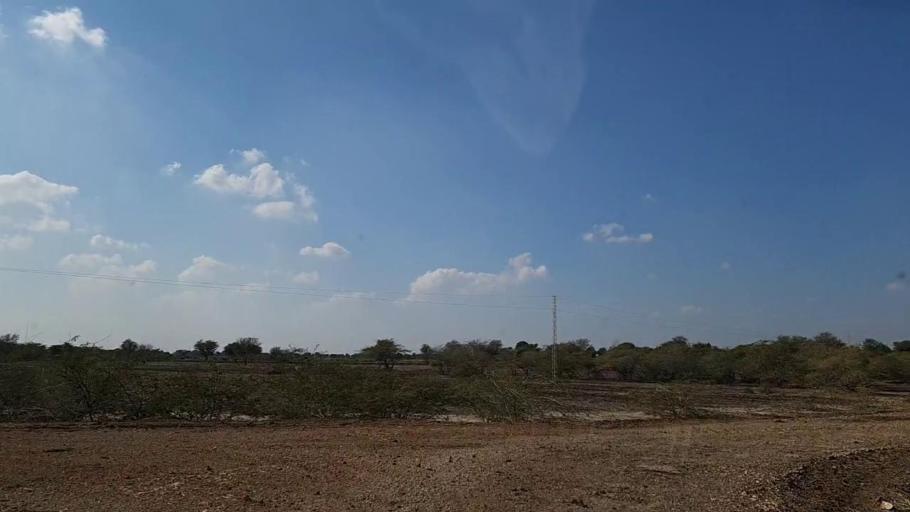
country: PK
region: Sindh
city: Pithoro
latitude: 25.6151
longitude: 69.3654
